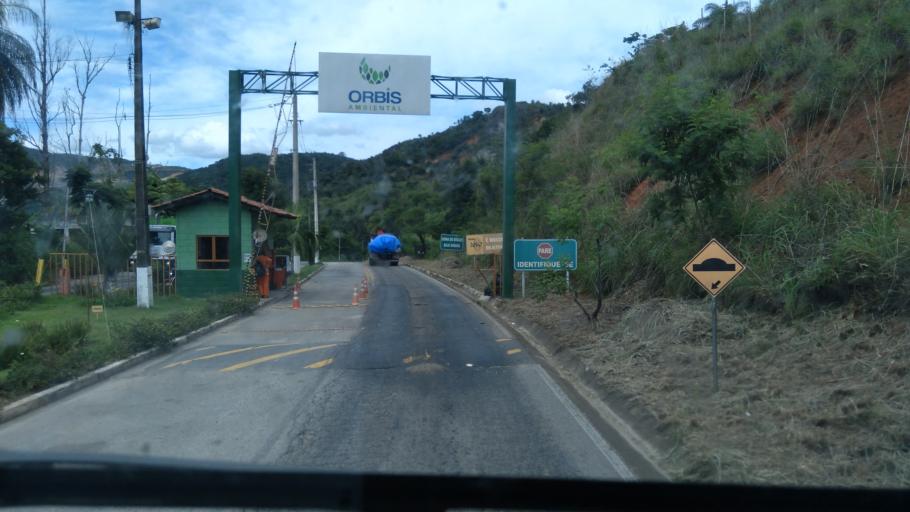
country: BR
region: Minas Gerais
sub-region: Belo Horizonte
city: Belo Horizonte
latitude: -19.8712
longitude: -43.8559
